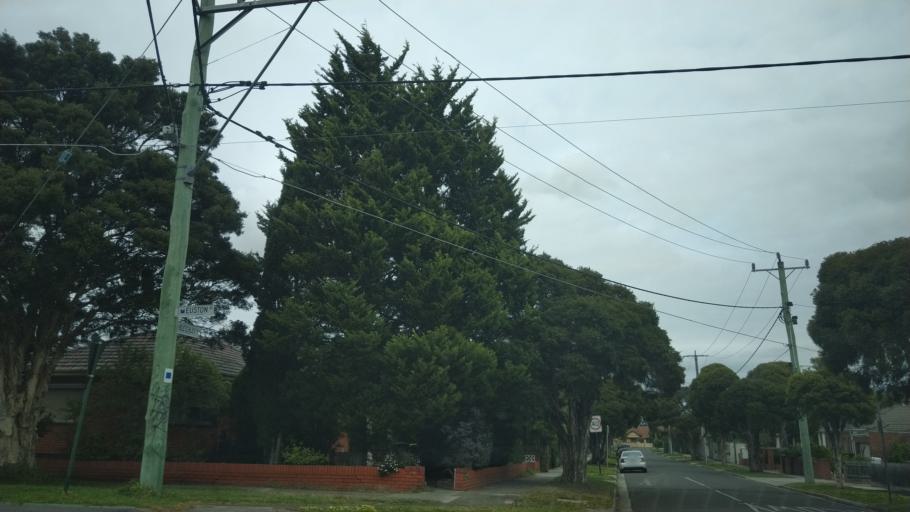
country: AU
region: Victoria
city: Hughesdale
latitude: -37.8944
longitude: 145.0825
